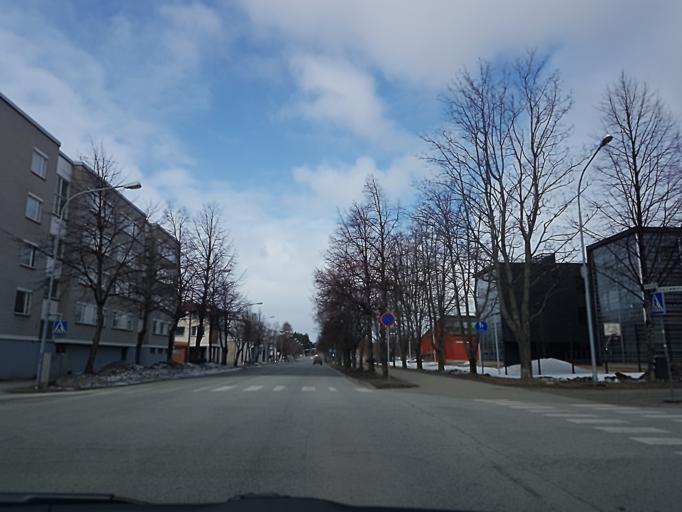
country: FI
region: North Karelia
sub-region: Joensuu
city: Joensuu
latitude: 62.6013
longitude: 29.7548
